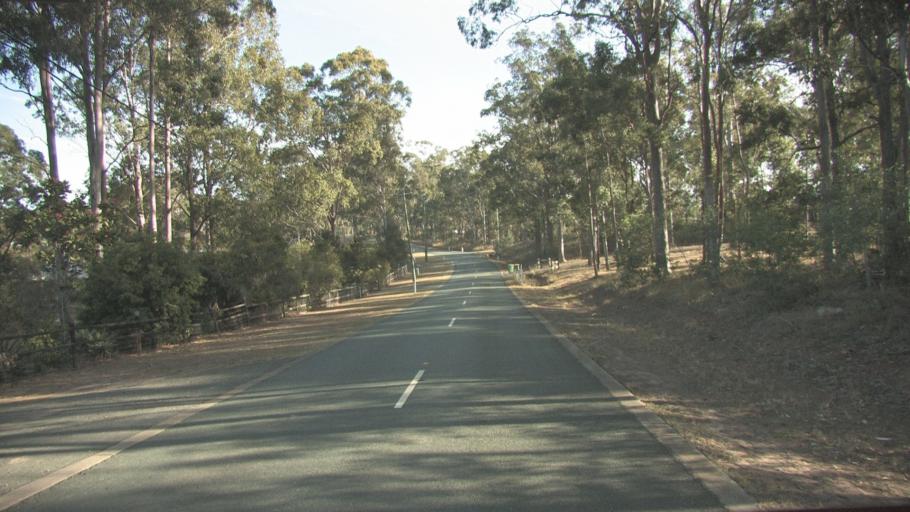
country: AU
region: Queensland
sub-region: Logan
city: Cedar Vale
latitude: -27.8847
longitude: 153.0086
